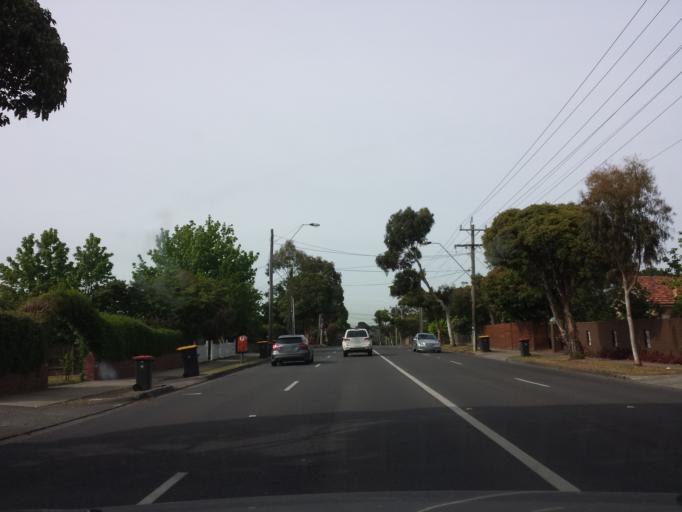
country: AU
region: Victoria
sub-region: Monash
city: Notting Hill
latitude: -37.8871
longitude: 145.1269
